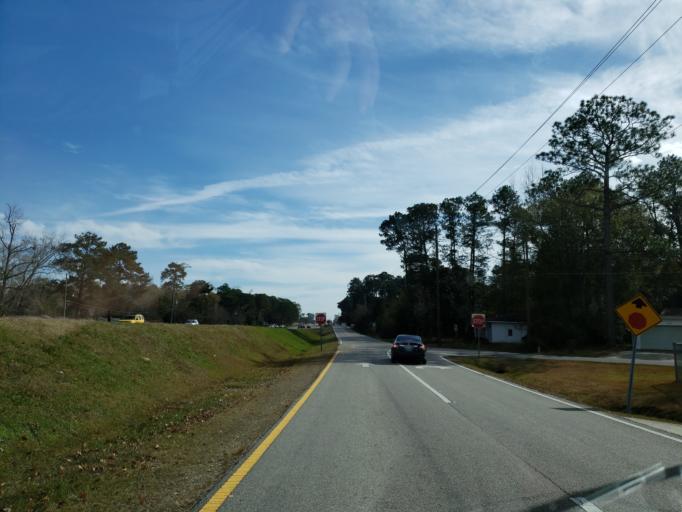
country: US
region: Mississippi
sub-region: Forrest County
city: Hattiesburg
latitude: 31.3173
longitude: -89.3272
